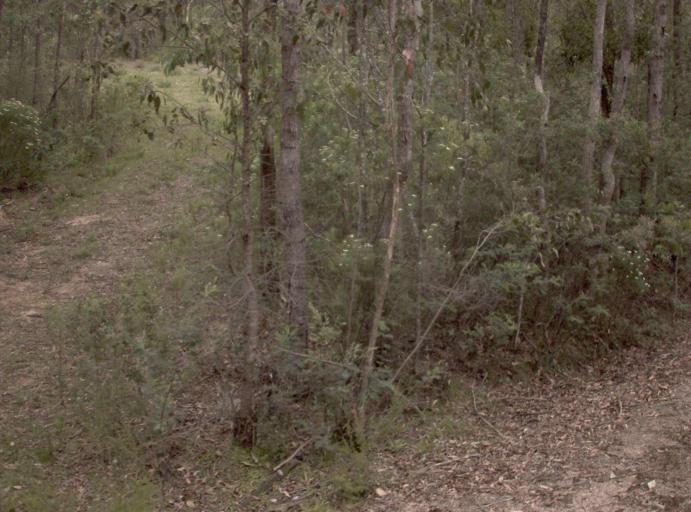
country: AU
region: Victoria
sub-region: East Gippsland
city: Bairnsdale
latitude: -37.6407
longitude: 147.2630
